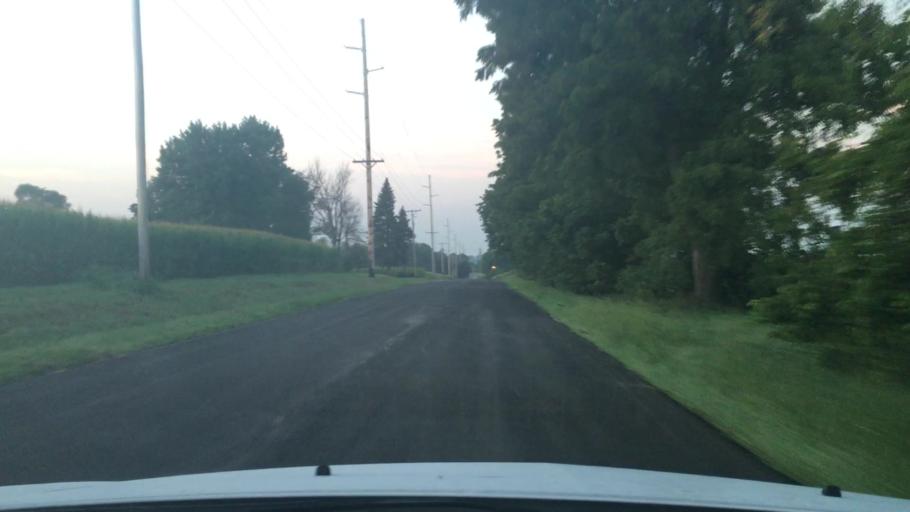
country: US
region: Illinois
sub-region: Ogle County
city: Rochelle
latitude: 41.9139
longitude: -89.0001
